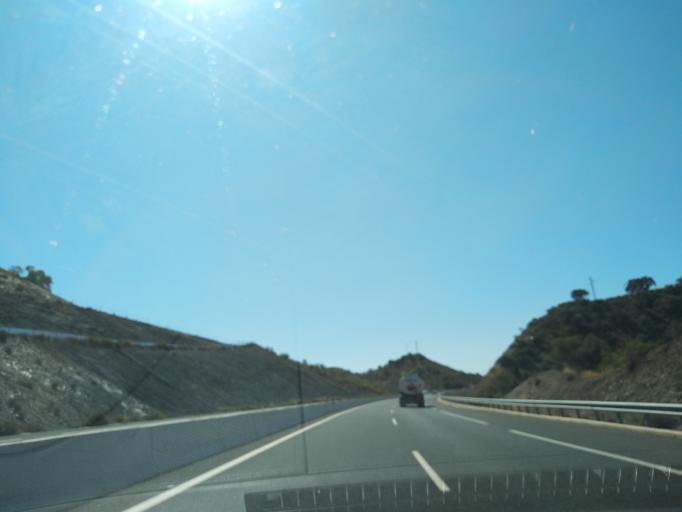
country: ES
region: Andalusia
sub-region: Provincia de Malaga
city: Almogia
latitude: 36.8286
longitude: -4.4699
